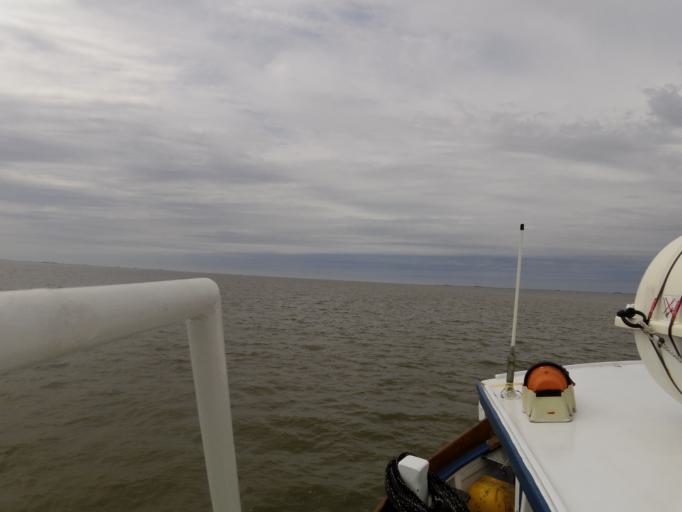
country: DE
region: Schleswig-Holstein
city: Langeness
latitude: 54.6137
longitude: 8.6308
